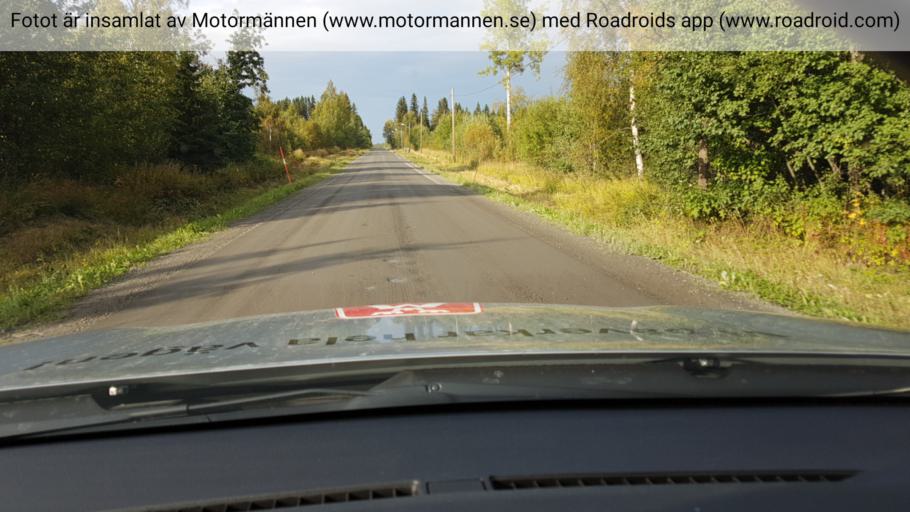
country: SE
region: Jaemtland
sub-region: Stroemsunds Kommun
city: Stroemsund
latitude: 64.0241
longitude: 15.8103
